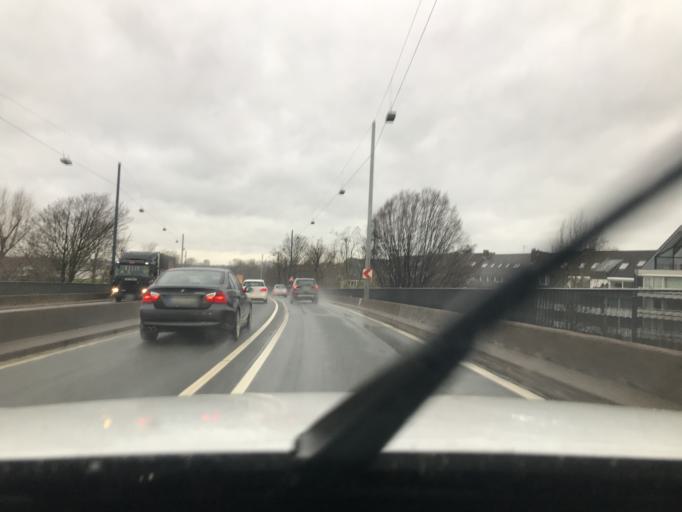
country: DE
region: North Rhine-Westphalia
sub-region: Regierungsbezirk Dusseldorf
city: Dusseldorf
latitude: 51.2256
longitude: 6.7577
